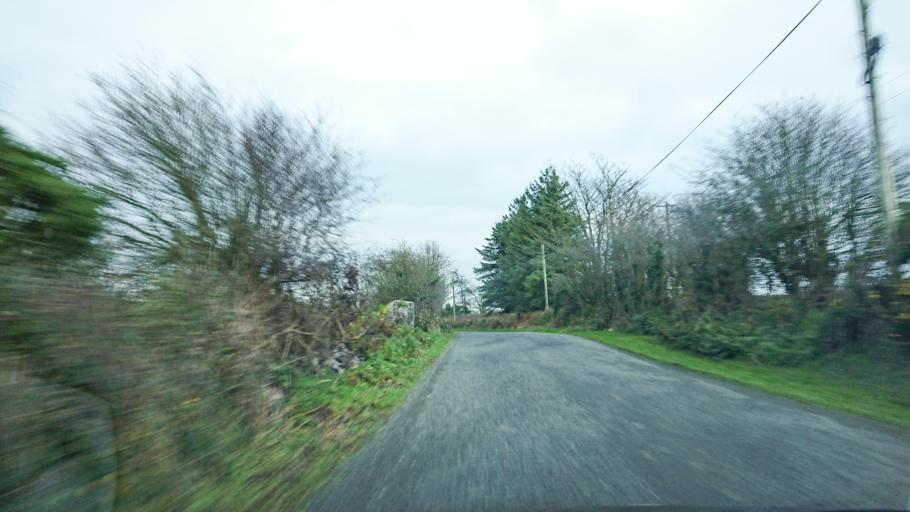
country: IE
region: Munster
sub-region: Waterford
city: Dunmore East
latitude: 52.2383
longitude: -6.9891
